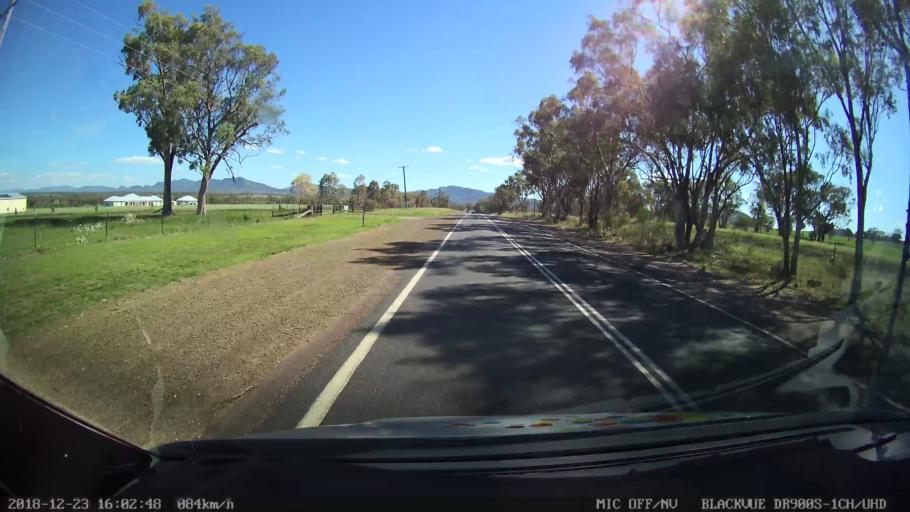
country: AU
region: New South Wales
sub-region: Tamworth Municipality
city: Phillip
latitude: -31.2362
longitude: 150.8061
